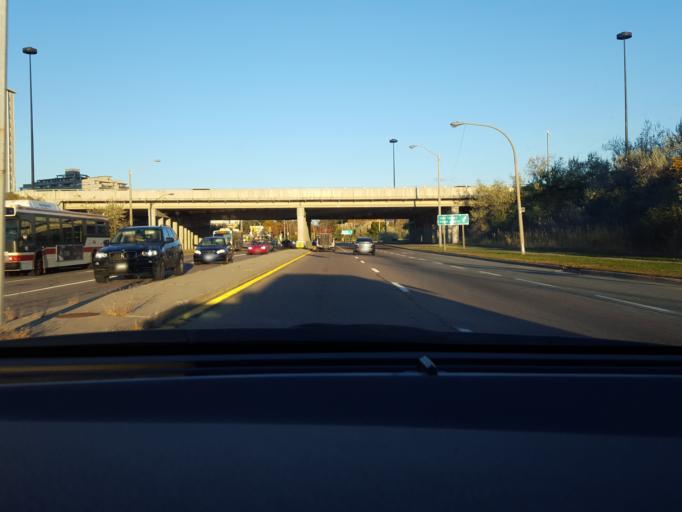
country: CA
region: Ontario
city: Willowdale
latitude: 43.7579
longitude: -79.3370
